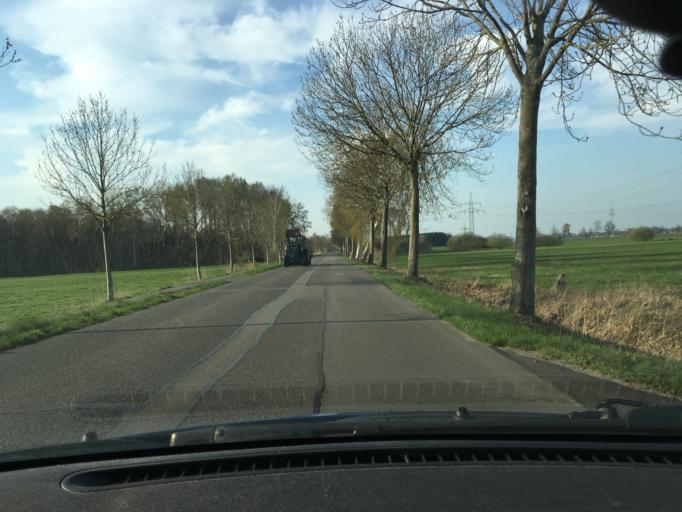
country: DE
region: Lower Saxony
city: Stelle
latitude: 53.4203
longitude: 10.0581
